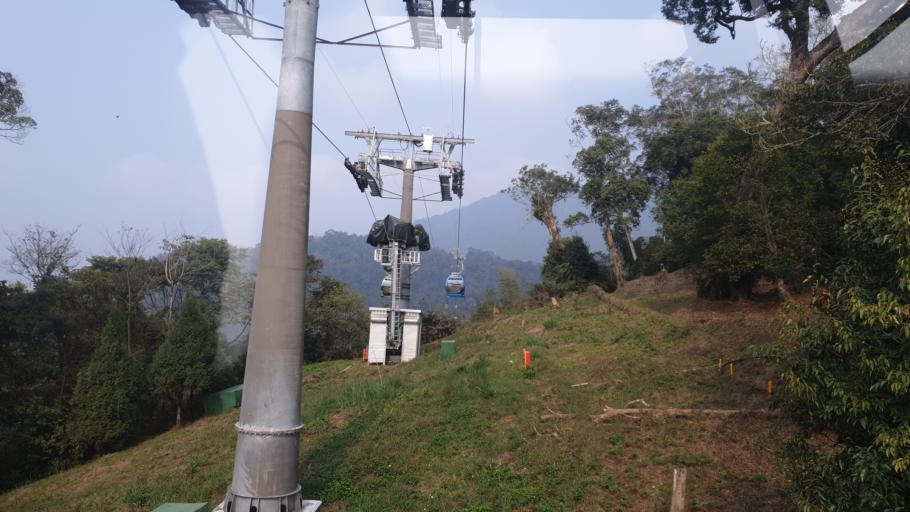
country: TW
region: Taiwan
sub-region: Nantou
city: Puli
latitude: 23.8552
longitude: 120.9410
